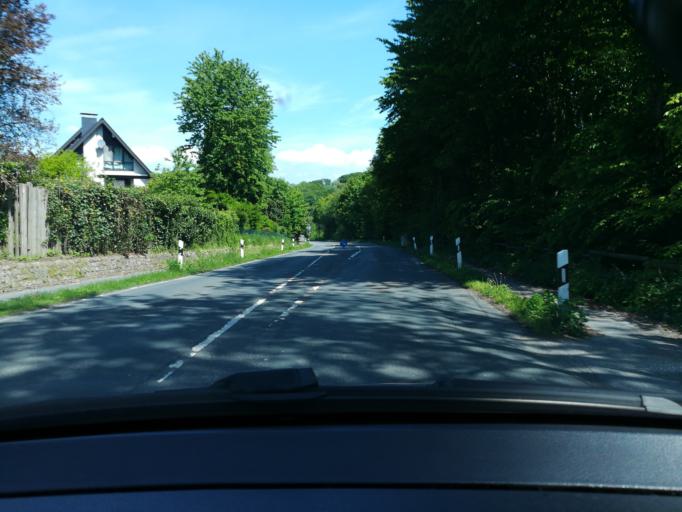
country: DE
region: North Rhine-Westphalia
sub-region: Regierungsbezirk Detmold
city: Oerlinghausen
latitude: 51.9737
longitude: 8.6194
